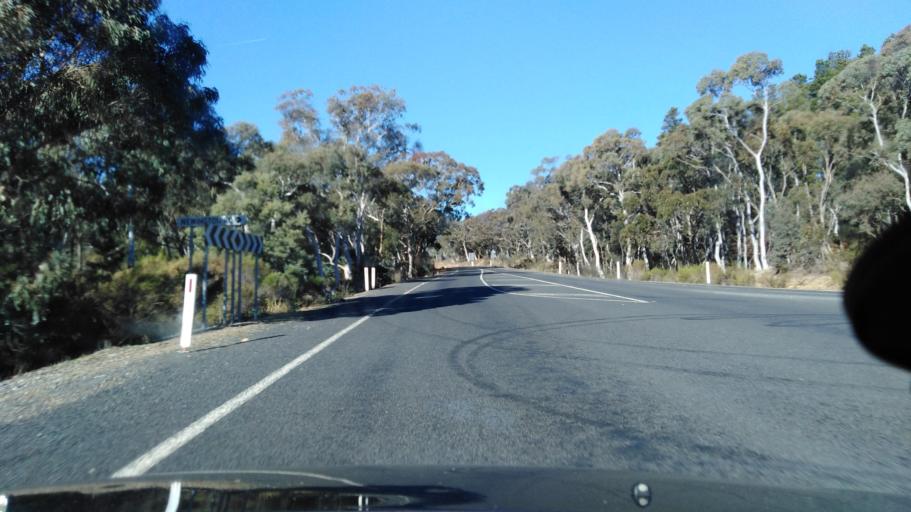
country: AU
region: New South Wales
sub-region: Palerang
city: Bungendore
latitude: -35.1857
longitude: 149.3173
